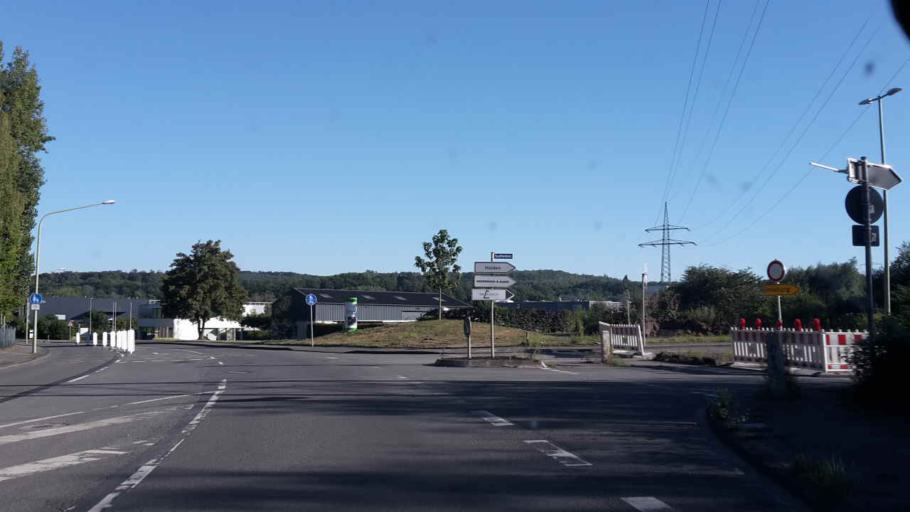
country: DE
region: North Rhine-Westphalia
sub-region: Regierungsbezirk Arnsberg
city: Hagen
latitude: 51.3775
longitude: 7.5254
